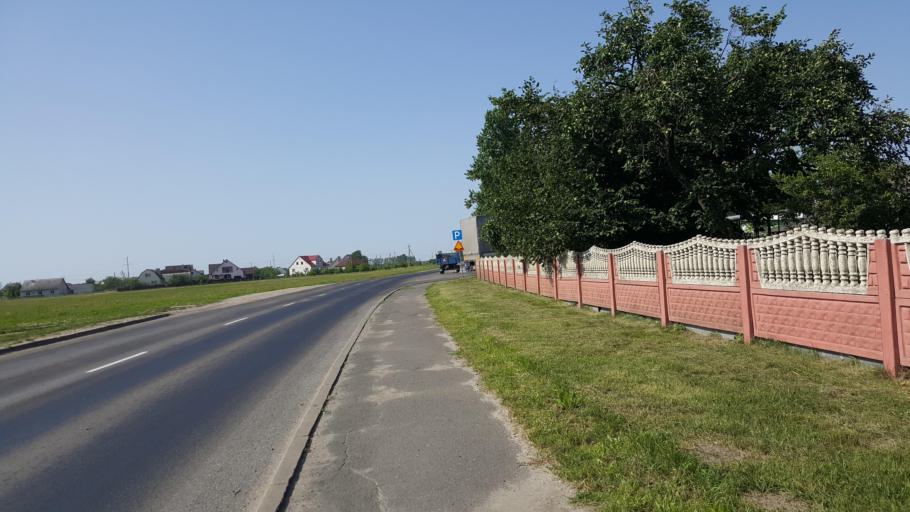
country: BY
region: Brest
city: Zhabinka
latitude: 52.2023
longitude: 24.0057
